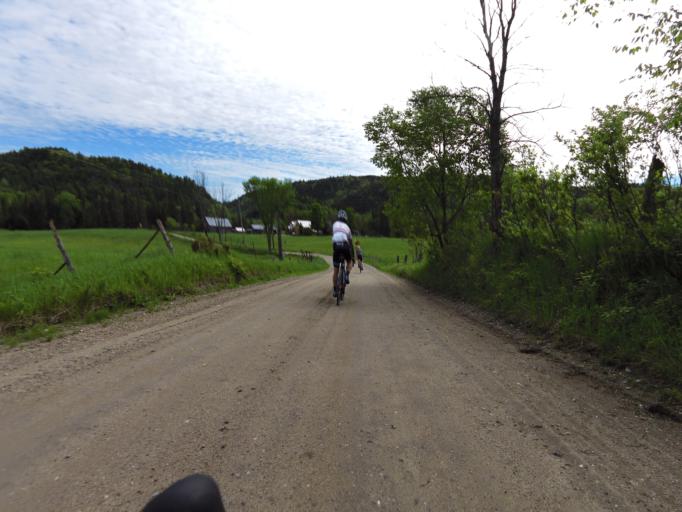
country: CA
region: Quebec
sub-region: Outaouais
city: Wakefield
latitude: 45.7732
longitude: -75.9249
